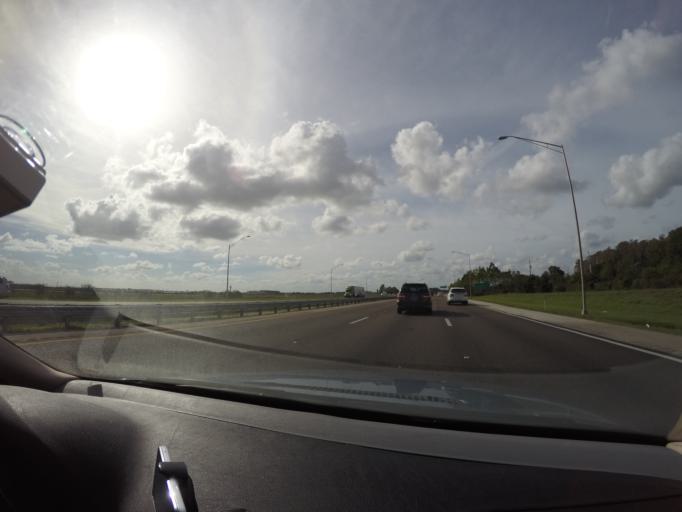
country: US
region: Florida
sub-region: Orange County
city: Conway
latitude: 28.4488
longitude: -81.2772
